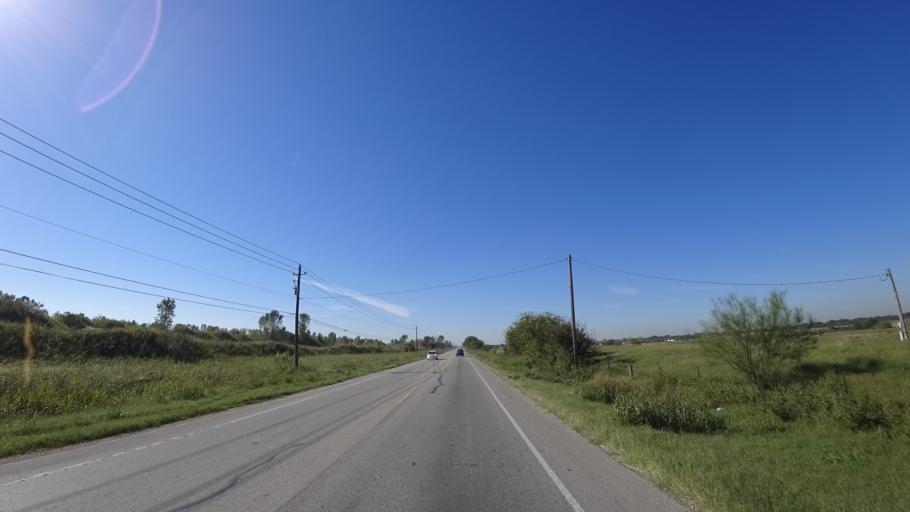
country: US
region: Texas
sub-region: Travis County
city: Hornsby Bend
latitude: 30.2516
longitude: -97.6153
